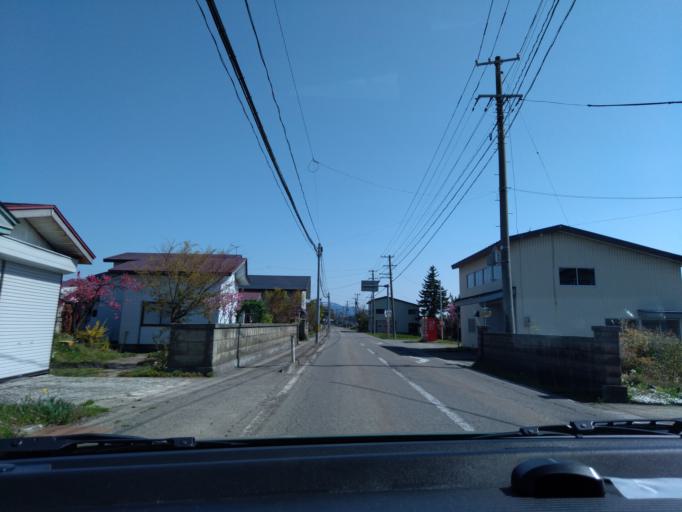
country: JP
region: Akita
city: Kakunodatemachi
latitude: 39.5215
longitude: 140.5883
